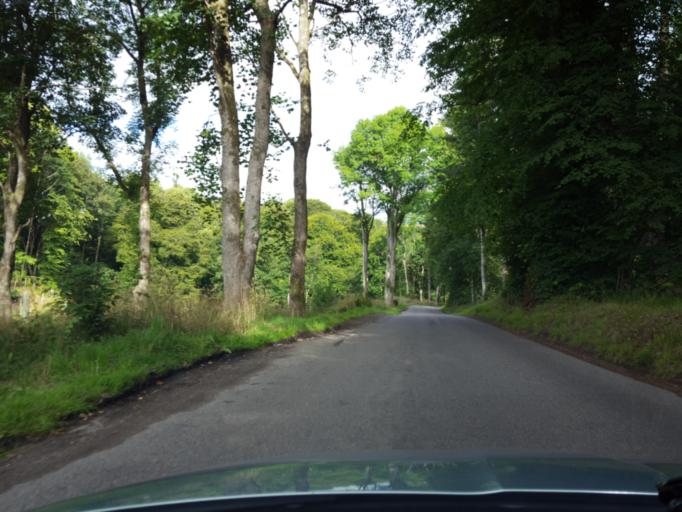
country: GB
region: Scotland
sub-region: Moray
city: Rothes
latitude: 57.4773
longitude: -3.1980
